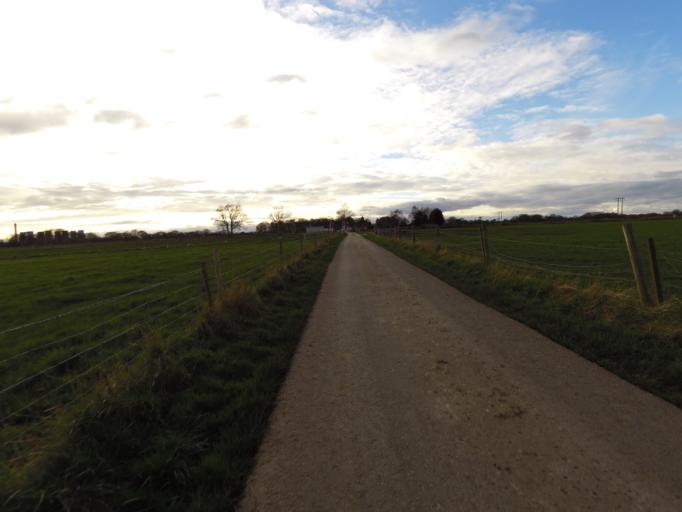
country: GB
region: England
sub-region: North Yorkshire
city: Brayton
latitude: 53.7344
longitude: -1.0803
